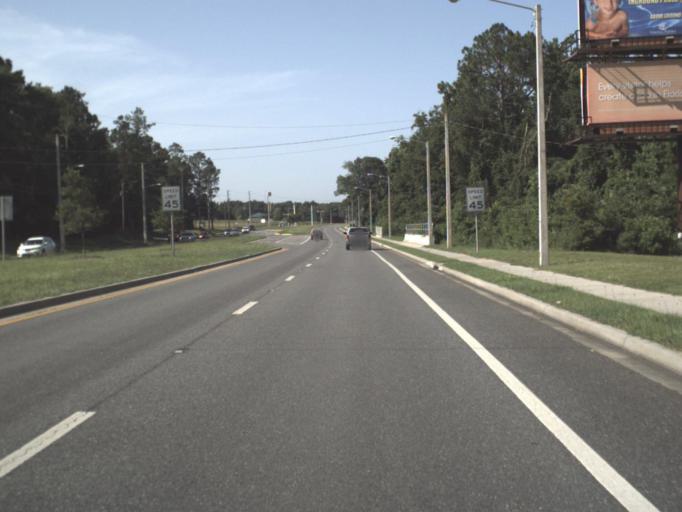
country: US
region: Florida
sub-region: Columbia County
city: Lake City
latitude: 30.1255
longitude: -82.6533
